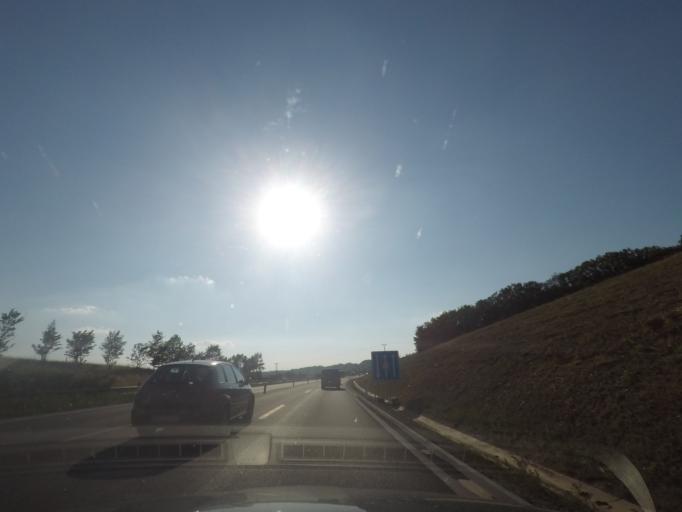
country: CZ
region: Olomoucky
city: Dolni Ujezd
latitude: 49.5468
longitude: 17.5603
